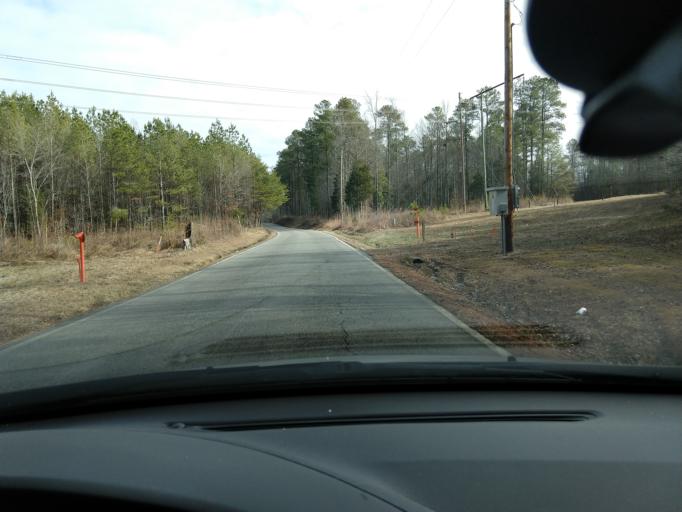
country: US
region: Virginia
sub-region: Henrico County
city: Fort Lee
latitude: 37.4301
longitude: -77.2705
